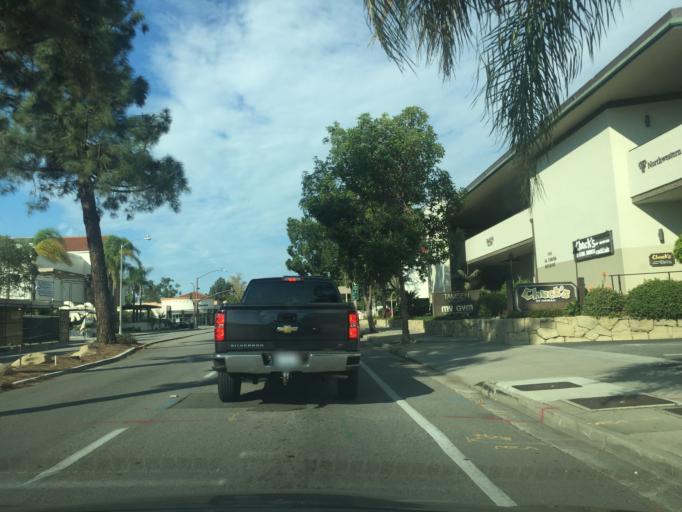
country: US
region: California
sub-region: Santa Barbara County
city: Mission Canyon
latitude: 34.4406
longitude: -119.7496
